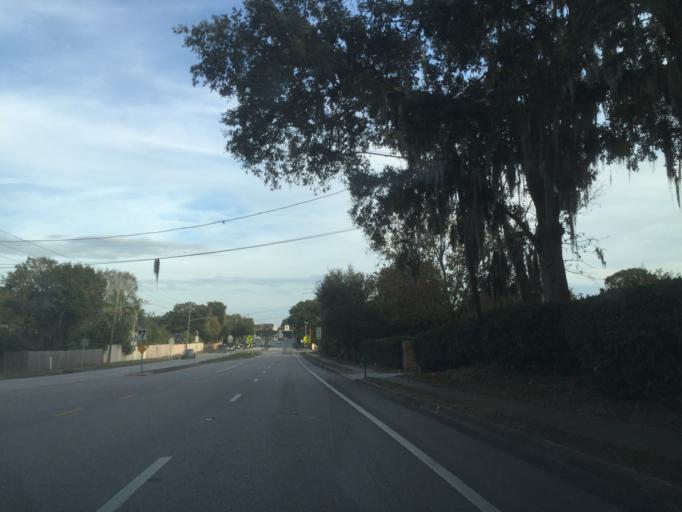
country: US
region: Florida
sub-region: Pinellas County
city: Safety Harbor
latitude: 27.9908
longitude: -82.7133
